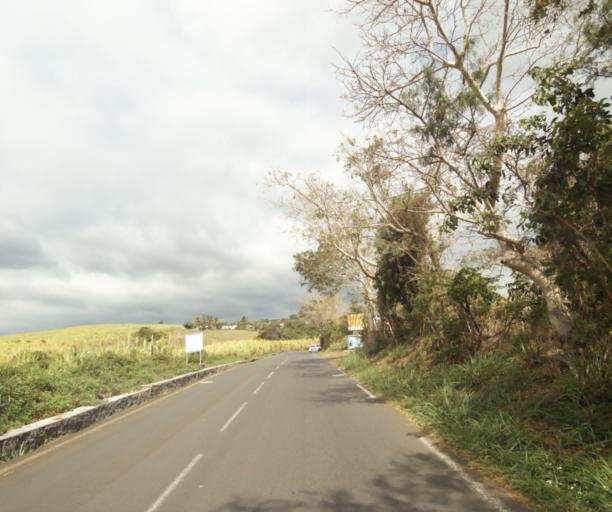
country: RE
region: Reunion
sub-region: Reunion
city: Saint-Paul
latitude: -21.0344
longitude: 55.2870
